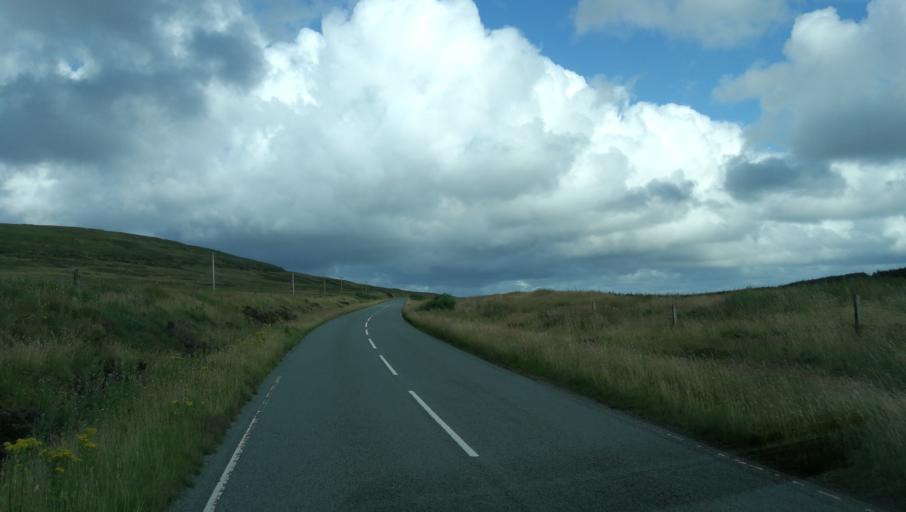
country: GB
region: Scotland
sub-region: Highland
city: Isle of Skye
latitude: 57.4691
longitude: -6.5264
